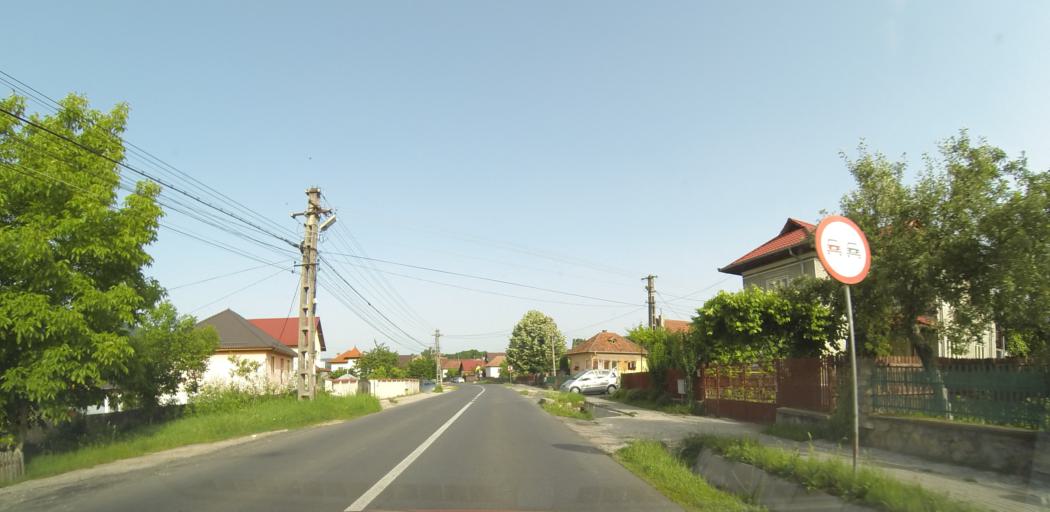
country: RO
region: Valcea
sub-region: Comuna Vladesti
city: Vladesti
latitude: 45.1212
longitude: 24.2999
